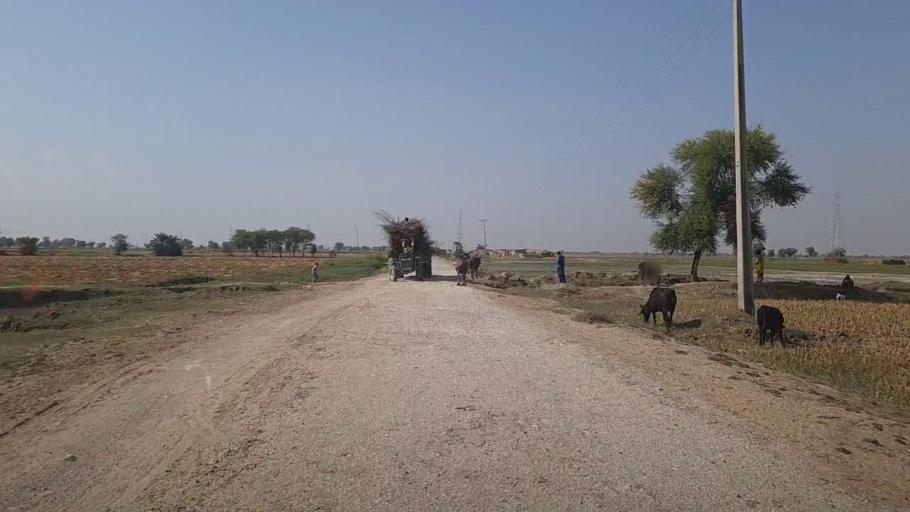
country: PK
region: Sindh
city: Kandhkot
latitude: 28.4078
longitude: 69.2501
